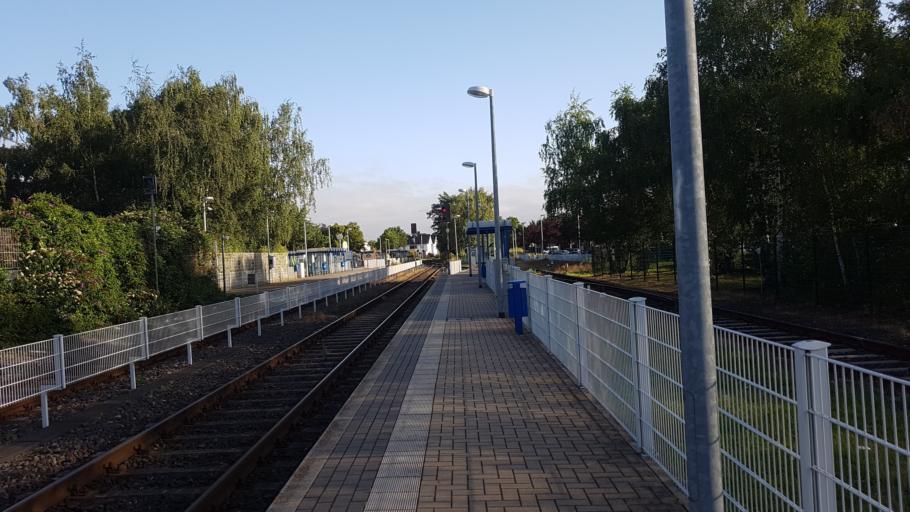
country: DE
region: North Rhine-Westphalia
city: Julich
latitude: 50.9181
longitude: 6.3683
